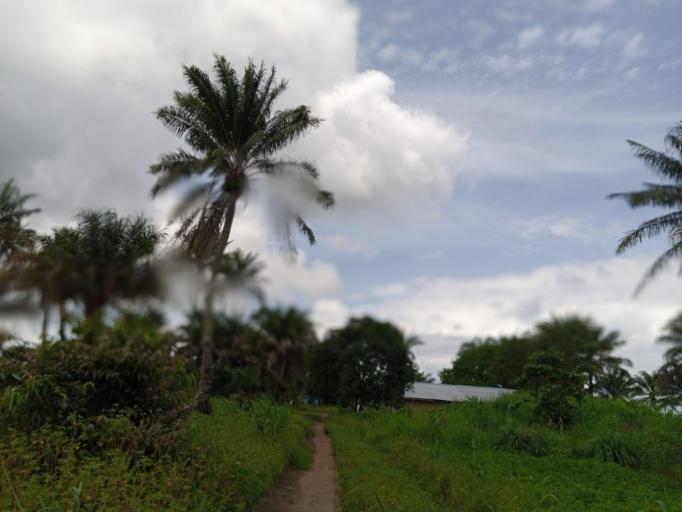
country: SL
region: Northern Province
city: Masoyila
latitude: 8.5891
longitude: -13.1718
